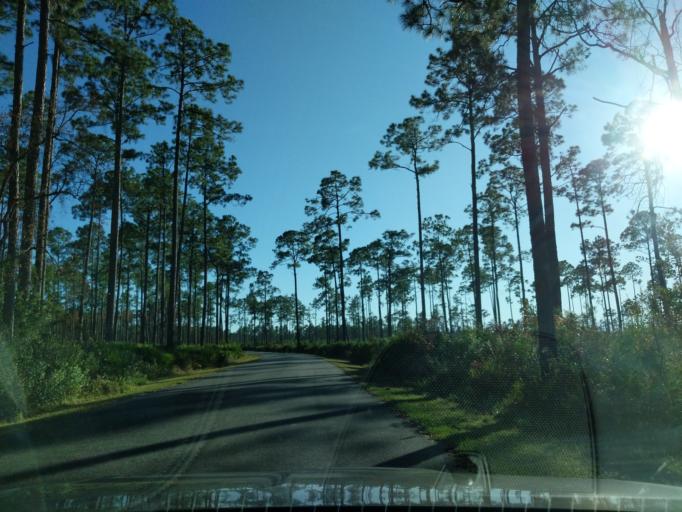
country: US
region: Georgia
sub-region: Charlton County
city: Folkston
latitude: 30.7253
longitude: -82.1397
